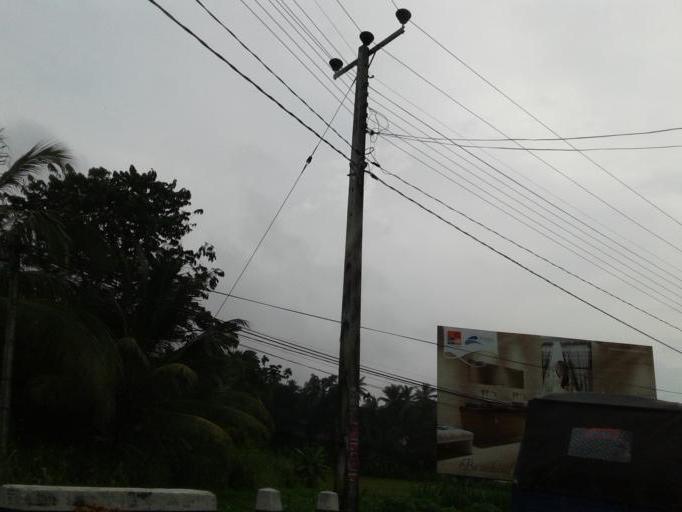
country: LK
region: Central
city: Kadugannawa
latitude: 7.2370
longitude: 80.3217
